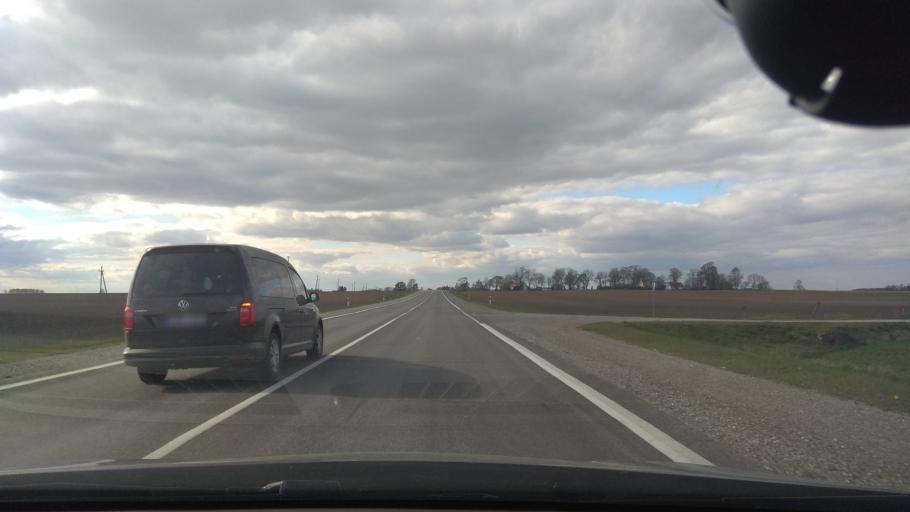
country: LT
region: Siauliu apskritis
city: Pakruojis
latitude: 55.7840
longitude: 24.0411
